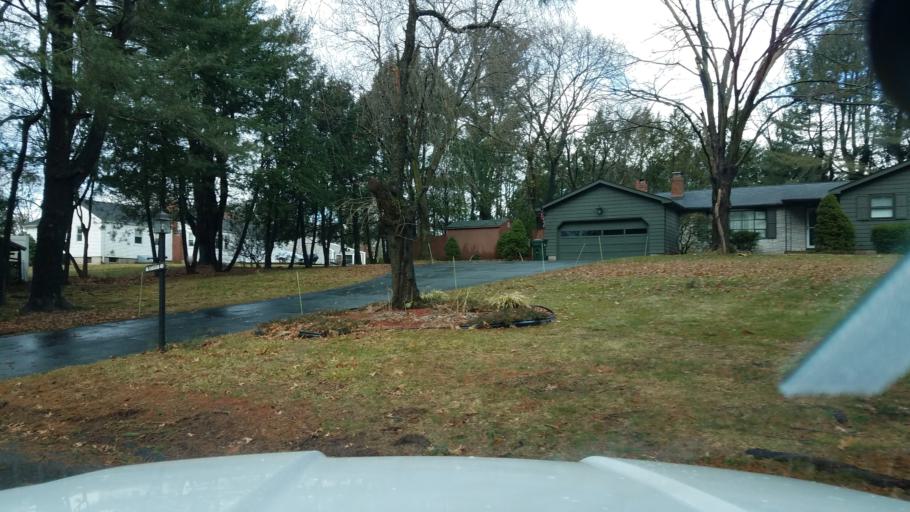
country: US
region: Connecticut
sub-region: Hartford County
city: Wethersfield
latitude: 41.6847
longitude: -72.6696
